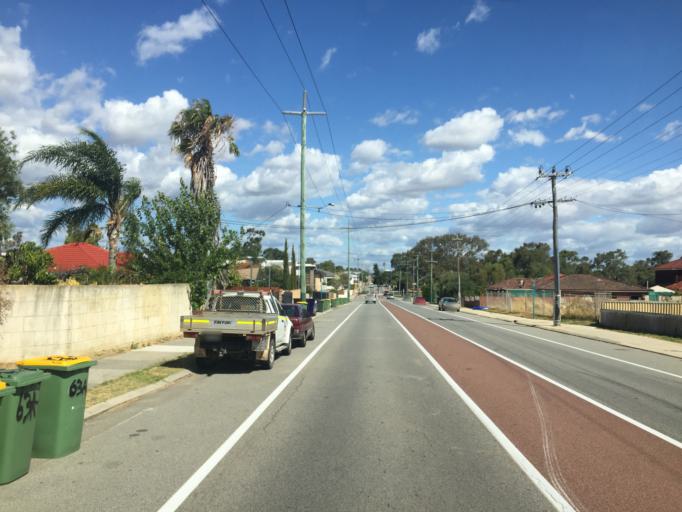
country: AU
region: Western Australia
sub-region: Belmont
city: Belmont
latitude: -31.9423
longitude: 115.9292
